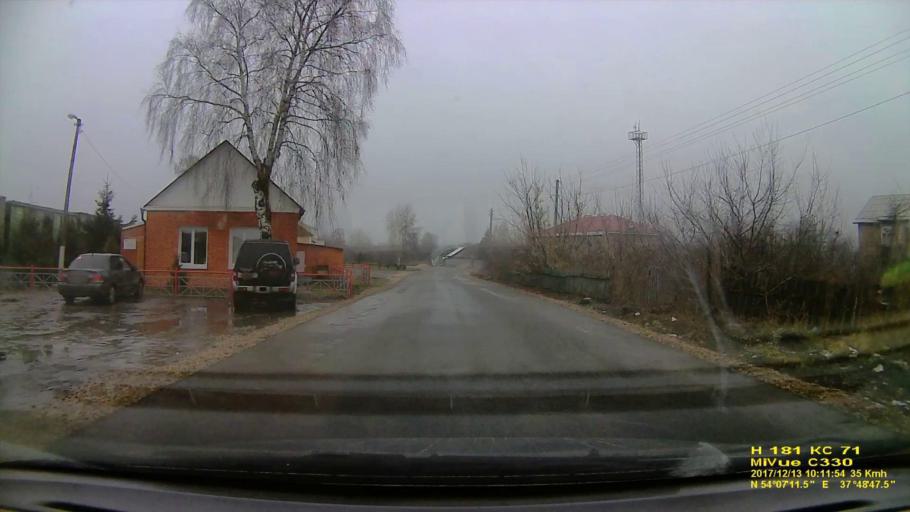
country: RU
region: Tula
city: Bolokhovo
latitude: 54.1199
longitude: 37.8131
